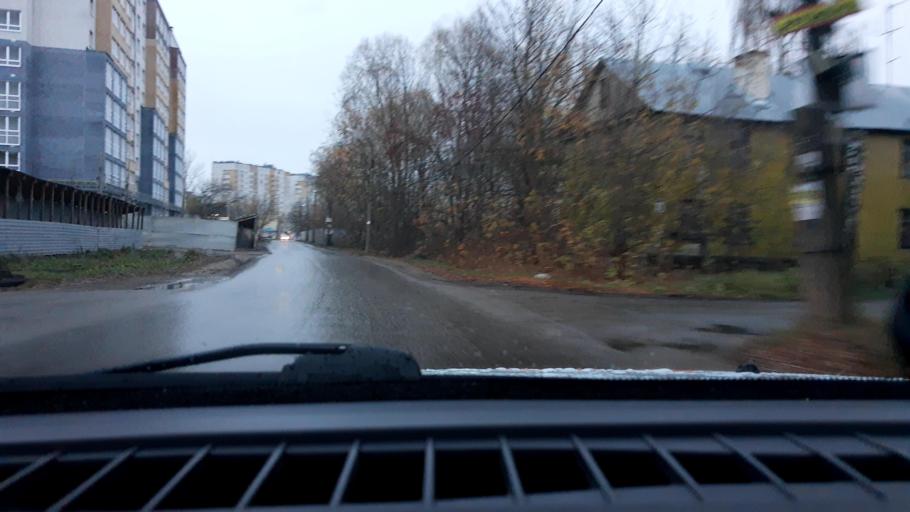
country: RU
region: Nizjnij Novgorod
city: Gorbatovka
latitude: 56.3436
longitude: 43.8303
